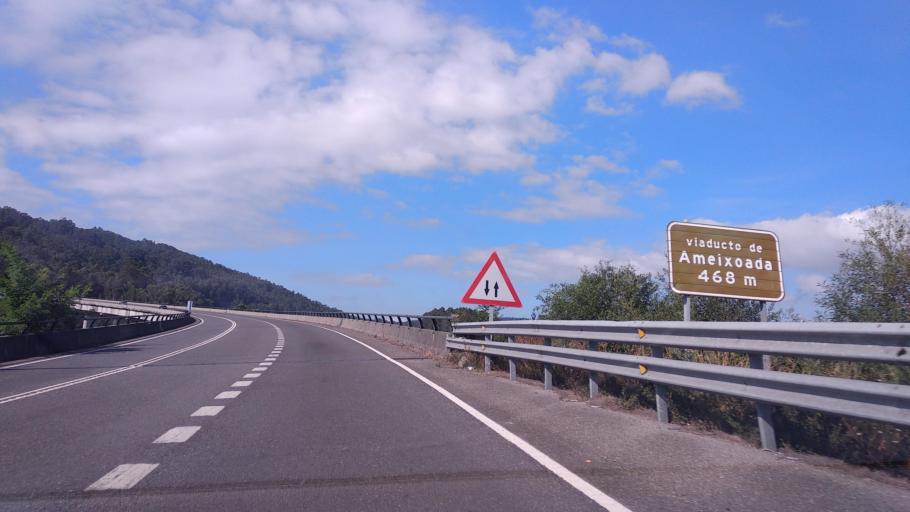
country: ES
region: Galicia
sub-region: Provincia de Pontevedra
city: Moana
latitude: 42.2798
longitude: -8.7521
